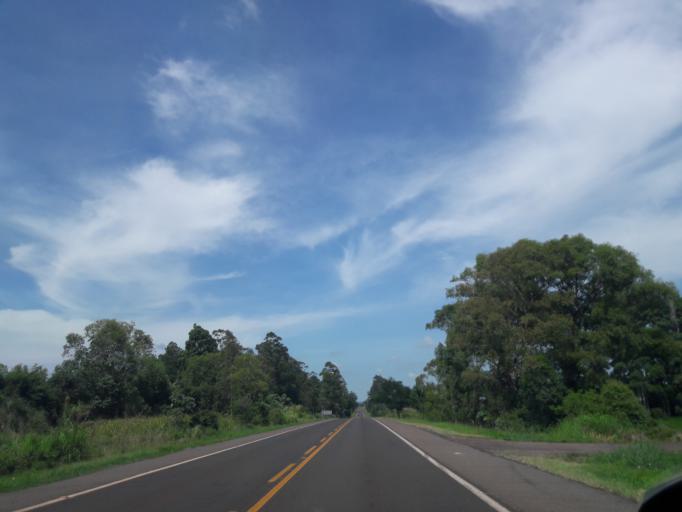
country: BR
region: Parana
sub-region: Campo Mourao
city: Campo Mourao
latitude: -24.2779
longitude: -52.5245
